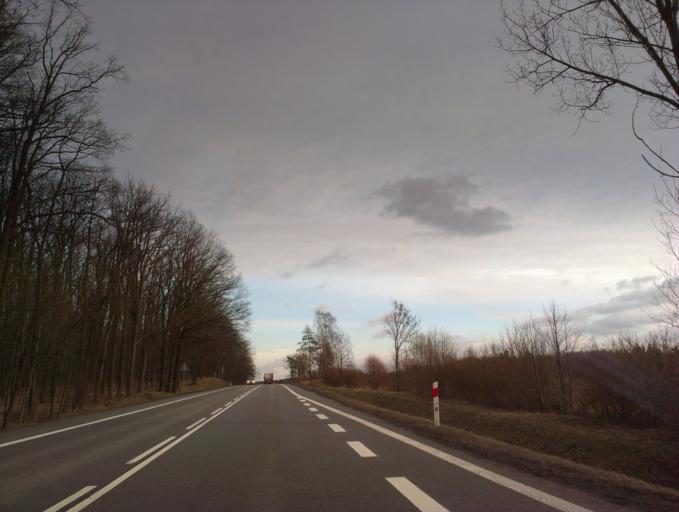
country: PL
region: Kujawsko-Pomorskie
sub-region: Powiat lipnowski
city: Skepe
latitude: 52.8575
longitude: 19.2883
